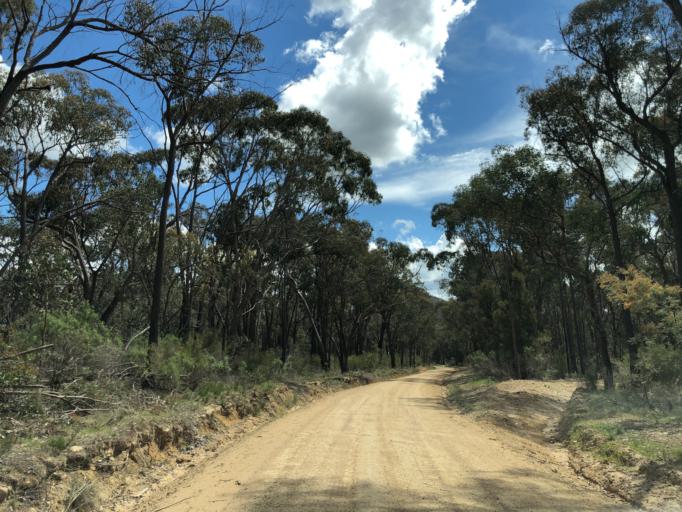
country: AU
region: Victoria
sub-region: Benalla
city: Benalla
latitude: -36.7378
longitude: 146.1521
